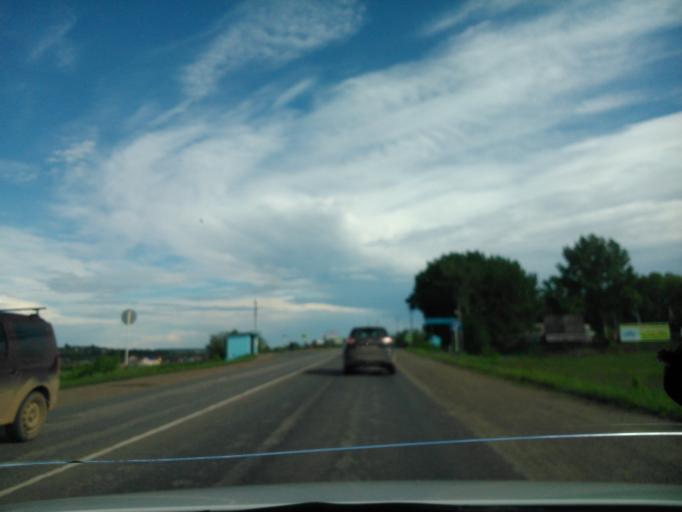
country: RU
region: Perm
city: Lobanovo
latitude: 57.8675
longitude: 56.2887
